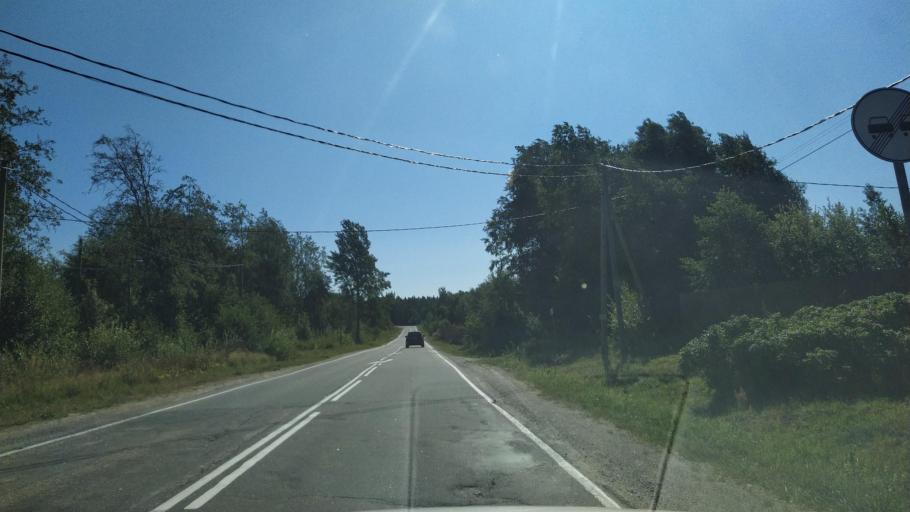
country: RU
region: Leningrad
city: Priozersk
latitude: 61.0043
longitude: 30.2240
